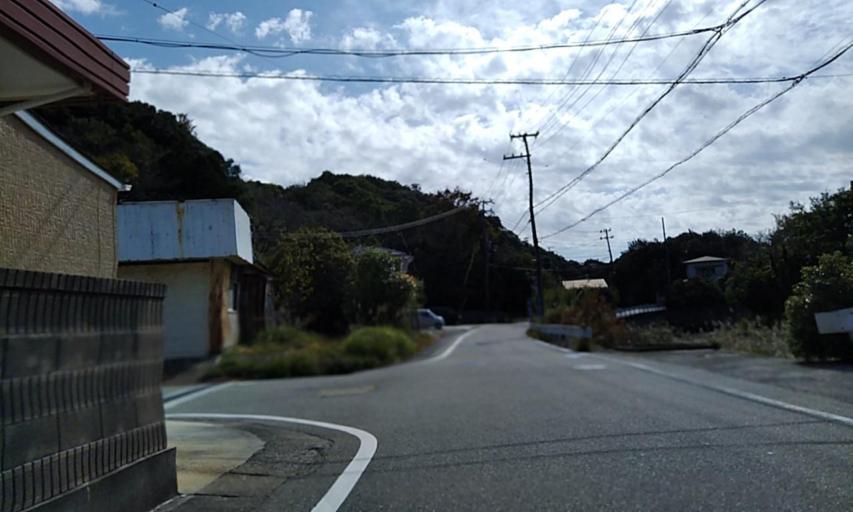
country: JP
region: Wakayama
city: Gobo
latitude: 33.9677
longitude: 135.1029
